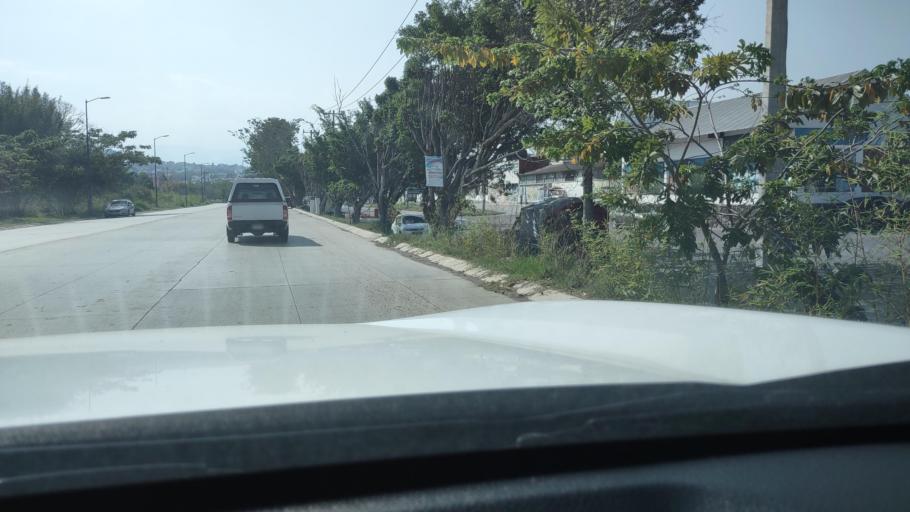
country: MX
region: Veracruz
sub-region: Emiliano Zapata
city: Las Trancas
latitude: 19.5136
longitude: -96.8547
